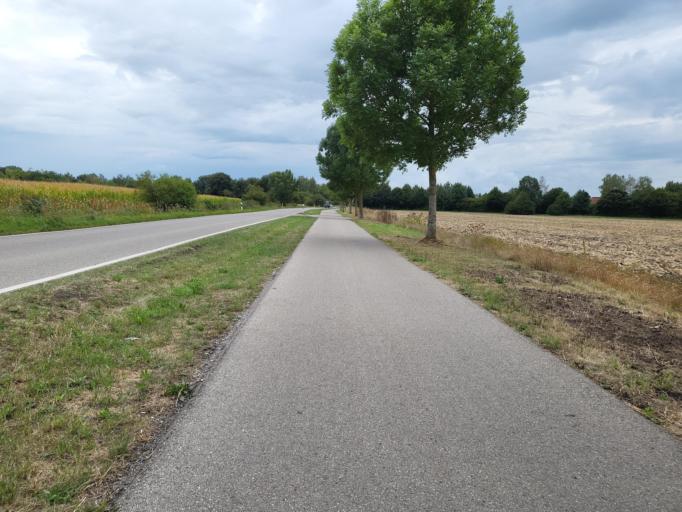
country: DE
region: Bavaria
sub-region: Upper Bavaria
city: Grobenzell
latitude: 48.2150
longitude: 11.3563
